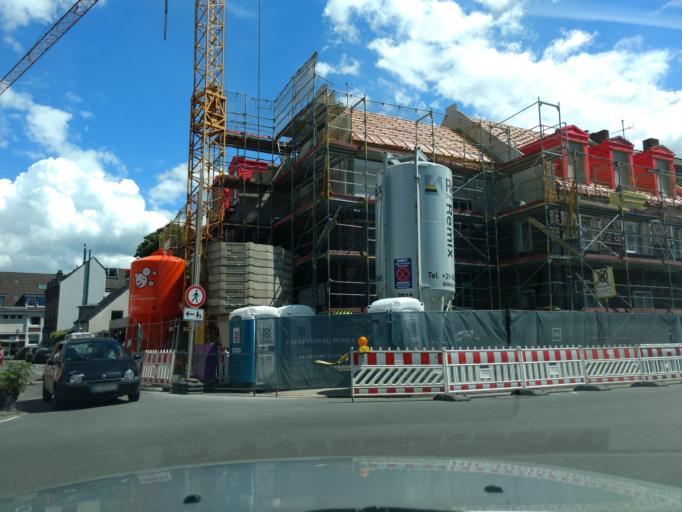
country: DE
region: North Rhine-Westphalia
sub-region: Regierungsbezirk Dusseldorf
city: Dusseldorf
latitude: 51.2397
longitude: 6.7517
